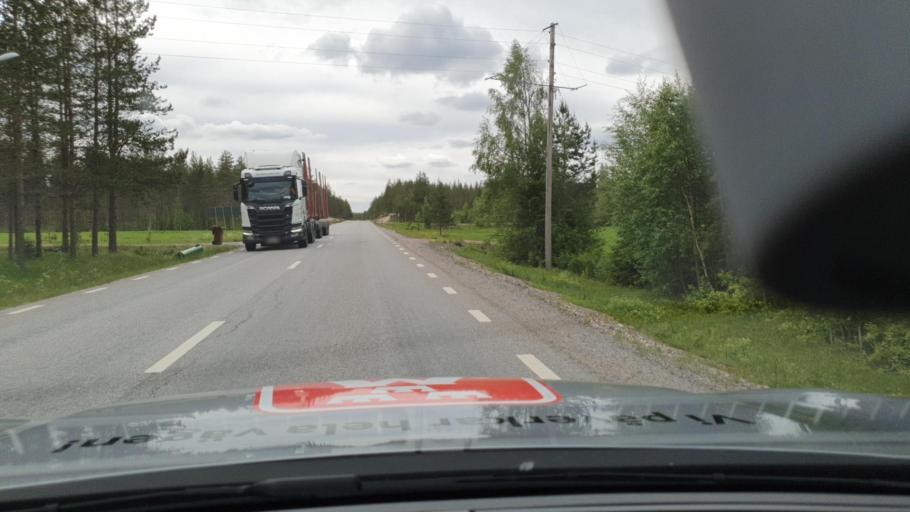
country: SE
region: Norrbotten
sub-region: Kalix Kommun
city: Kalix
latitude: 65.9653
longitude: 23.4572
